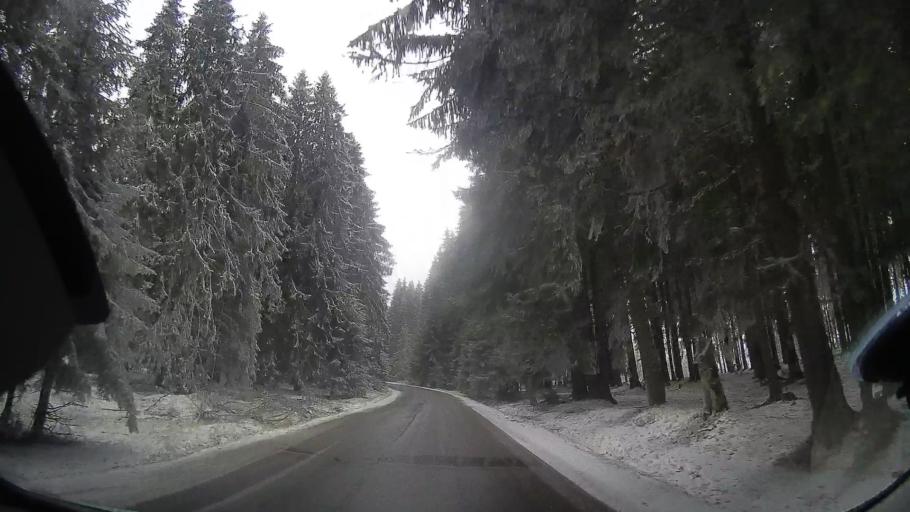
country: RO
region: Cluj
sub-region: Comuna Belis
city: Belis
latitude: 46.6437
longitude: 23.0592
